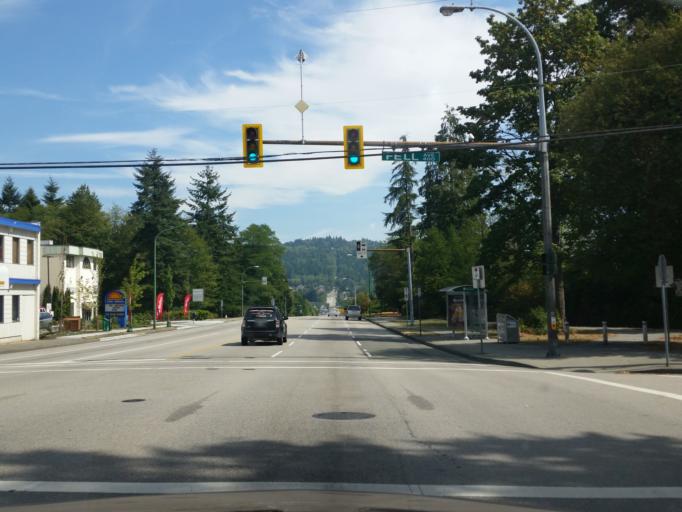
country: CA
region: British Columbia
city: Burnaby
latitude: 49.2803
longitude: -122.9757
